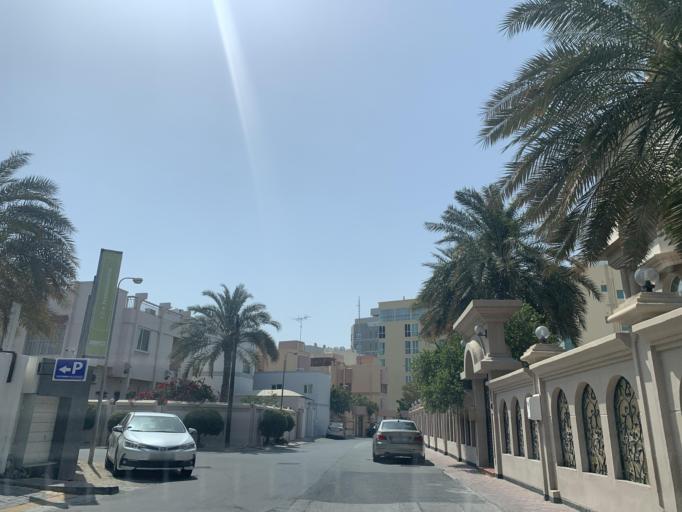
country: BH
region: Manama
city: Manama
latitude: 26.2070
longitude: 50.5803
